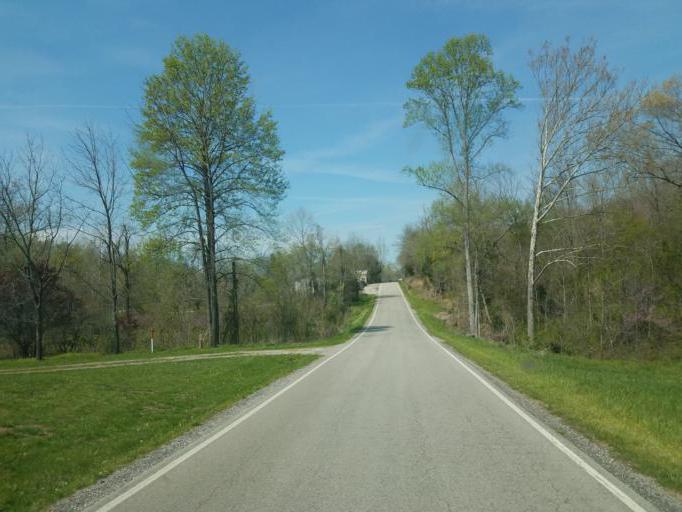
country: US
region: Kentucky
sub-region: Edmonson County
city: Brownsville
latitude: 37.3036
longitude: -86.4216
